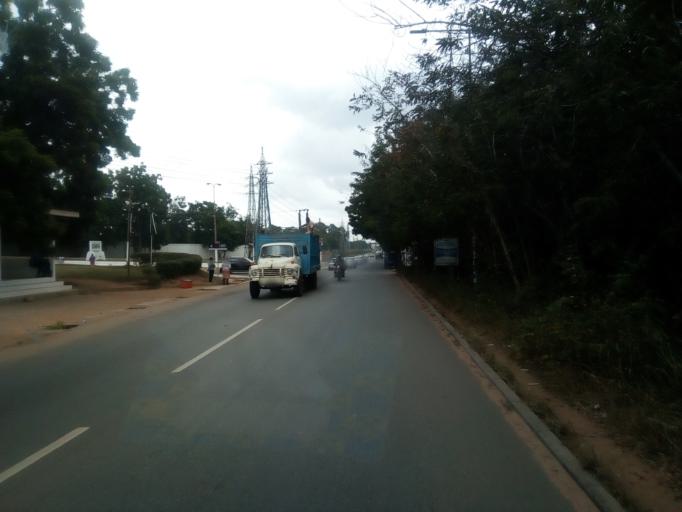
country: GH
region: Greater Accra
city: Dome
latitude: 5.6416
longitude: -0.2050
